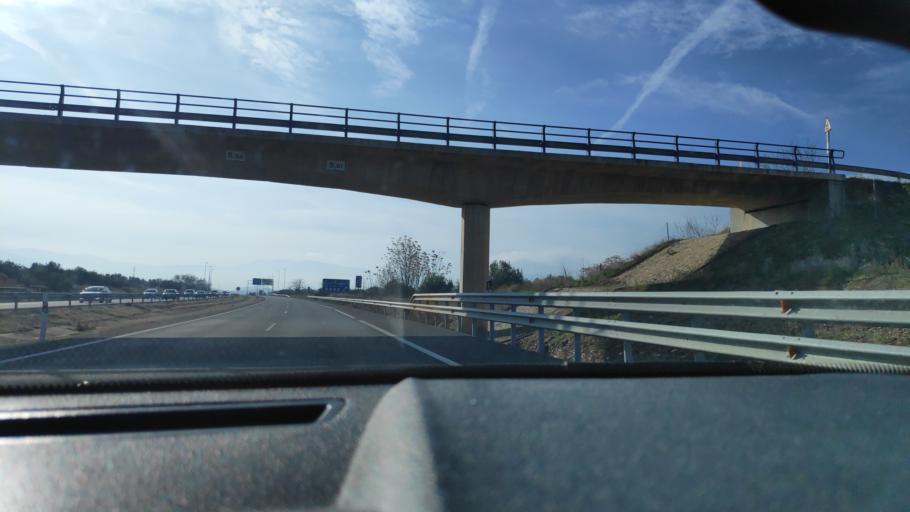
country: ES
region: Andalusia
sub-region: Provincia de Jaen
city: Jaen
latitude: 37.8291
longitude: -3.7662
